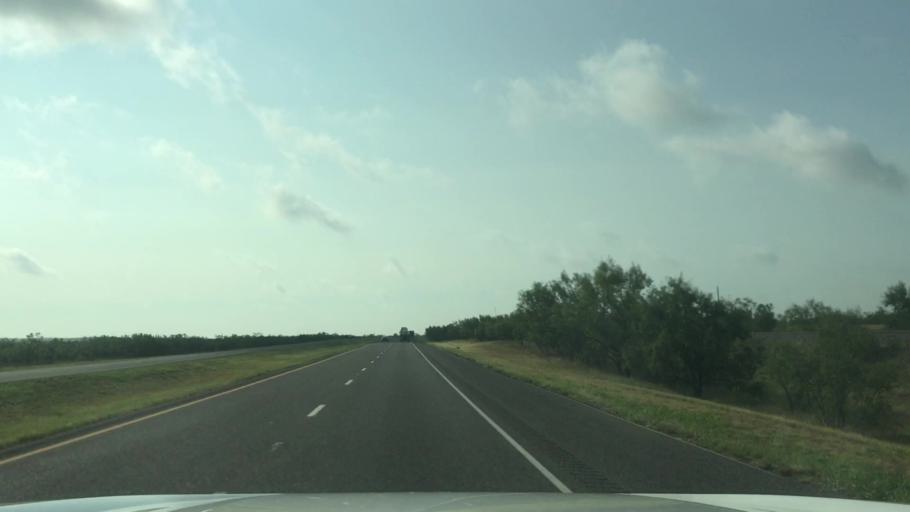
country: US
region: Texas
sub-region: Scurry County
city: Snyder
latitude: 32.8364
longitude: -100.9916
